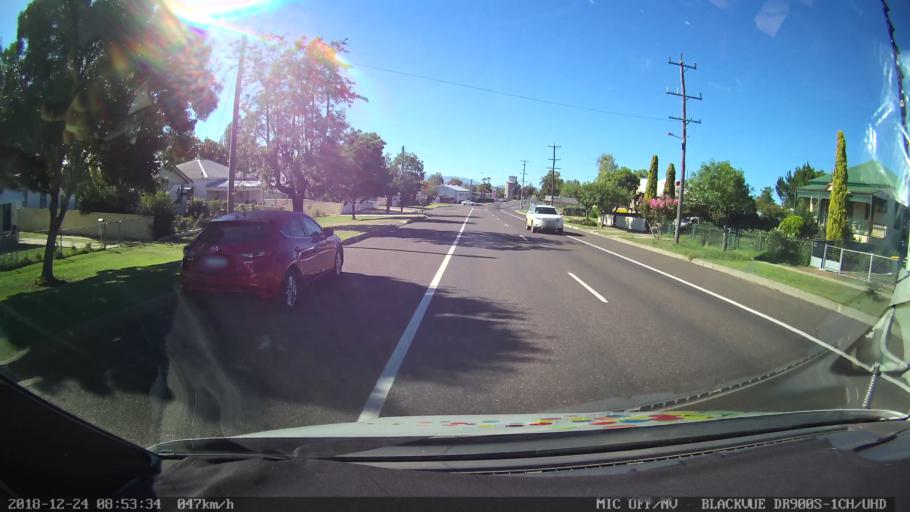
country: AU
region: New South Wales
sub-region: Liverpool Plains
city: Quirindi
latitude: -31.4994
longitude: 150.6812
